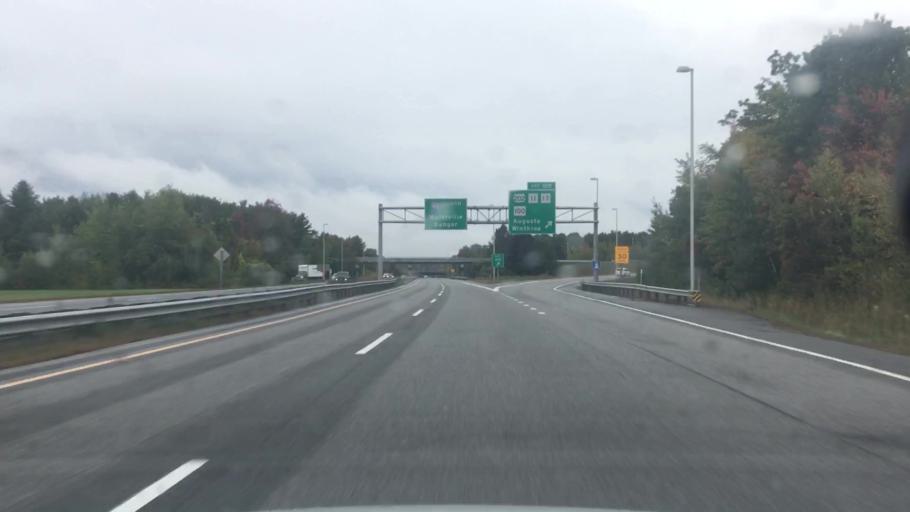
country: US
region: Maine
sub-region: Kennebec County
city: Augusta
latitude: 44.3106
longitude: -69.8086
